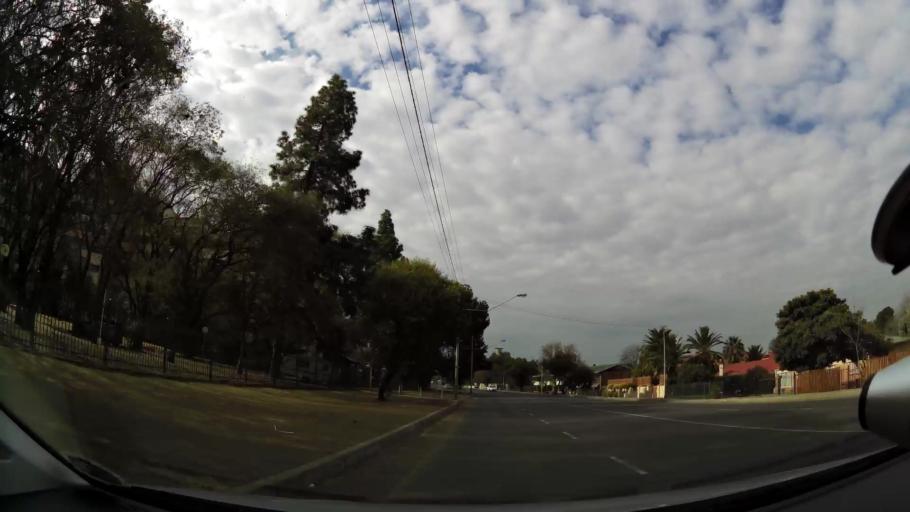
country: ZA
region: Orange Free State
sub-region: Mangaung Metropolitan Municipality
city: Bloemfontein
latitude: -29.1069
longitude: 26.2354
